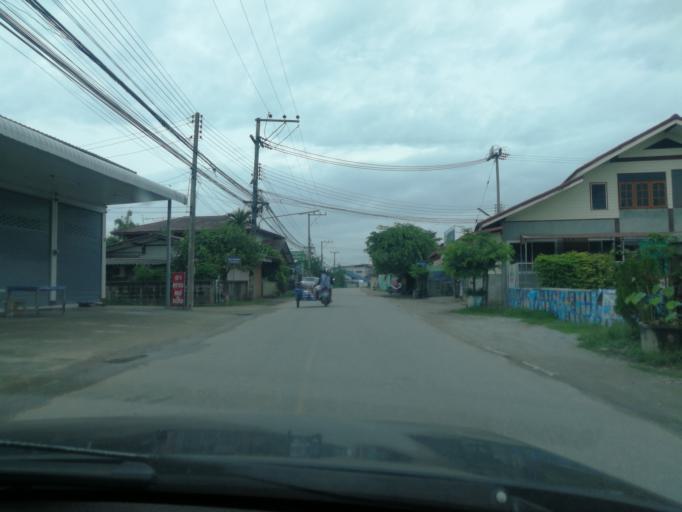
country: TH
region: Chiang Mai
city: San Pa Tong
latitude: 18.5969
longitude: 98.9105
